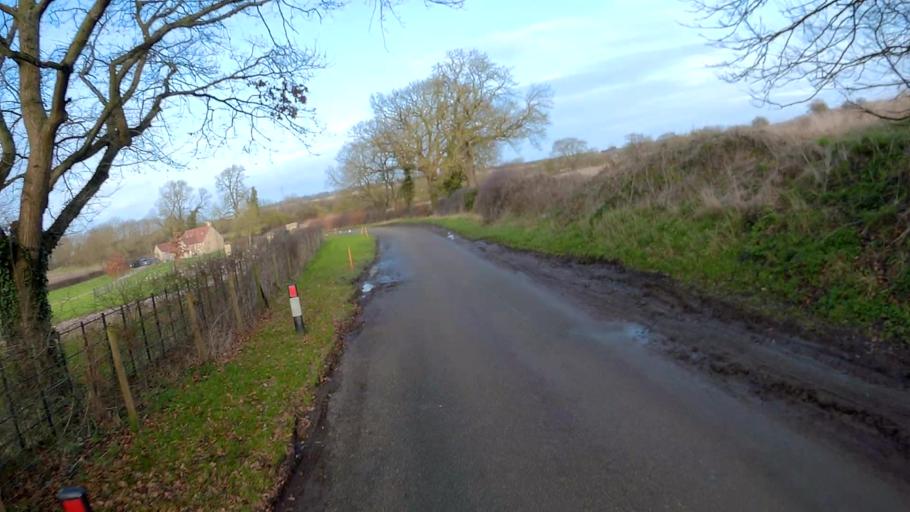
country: GB
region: England
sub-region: Lincolnshire
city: Bourne
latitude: 52.7520
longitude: -0.4160
